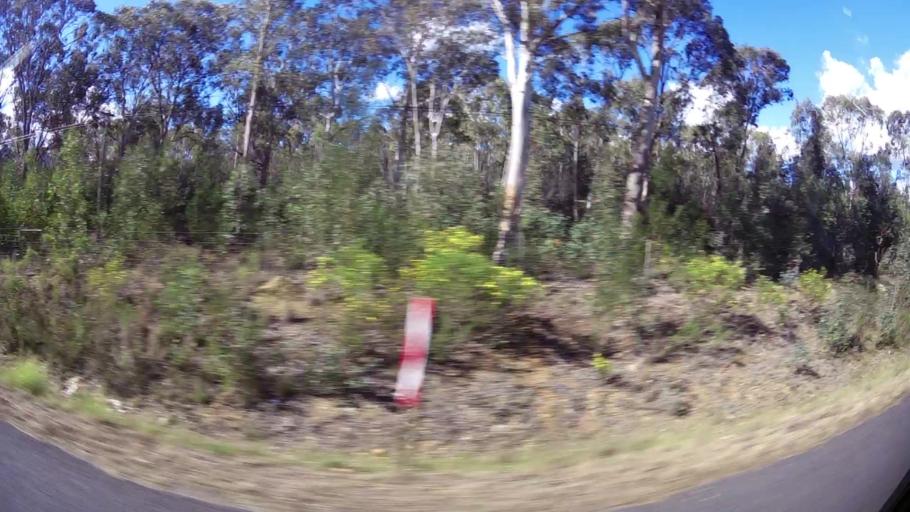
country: ZA
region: Western Cape
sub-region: Overberg District Municipality
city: Swellendam
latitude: -34.0299
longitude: 20.4205
